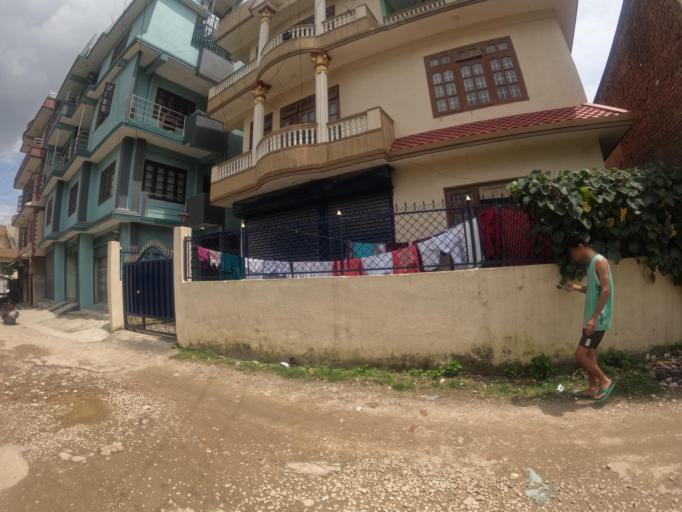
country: NP
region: Central Region
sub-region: Bagmati Zone
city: Bhaktapur
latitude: 27.6859
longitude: 85.3779
